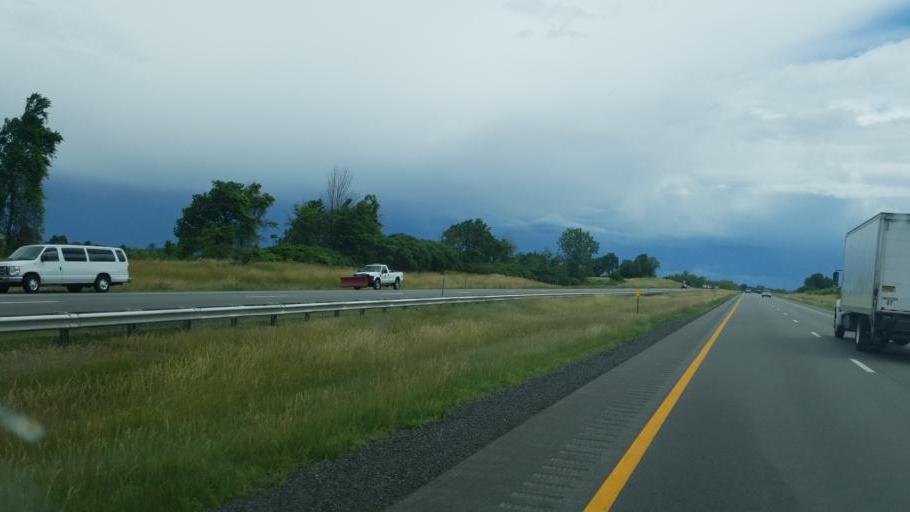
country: US
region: New York
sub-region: Monroe County
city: Scottsville
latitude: 43.0375
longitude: -77.8080
